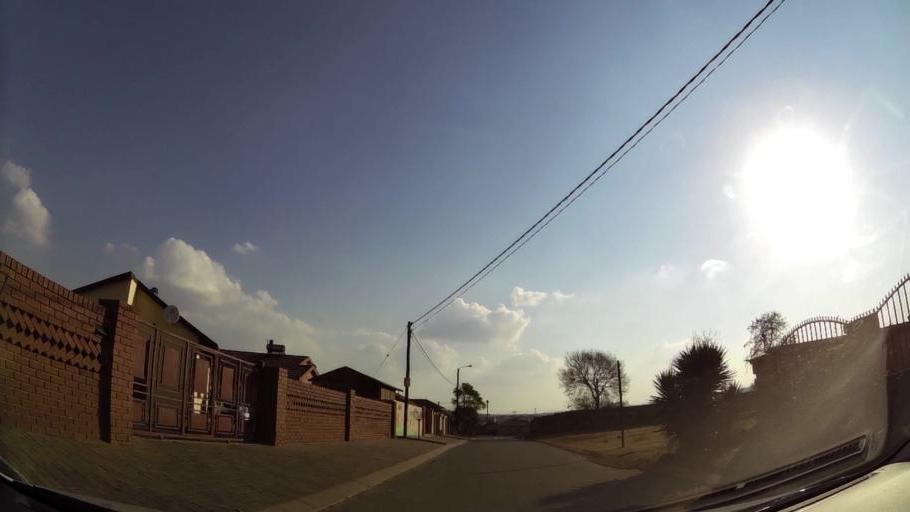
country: ZA
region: Gauteng
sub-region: Ekurhuleni Metropolitan Municipality
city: Tembisa
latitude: -25.9525
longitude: 28.2115
